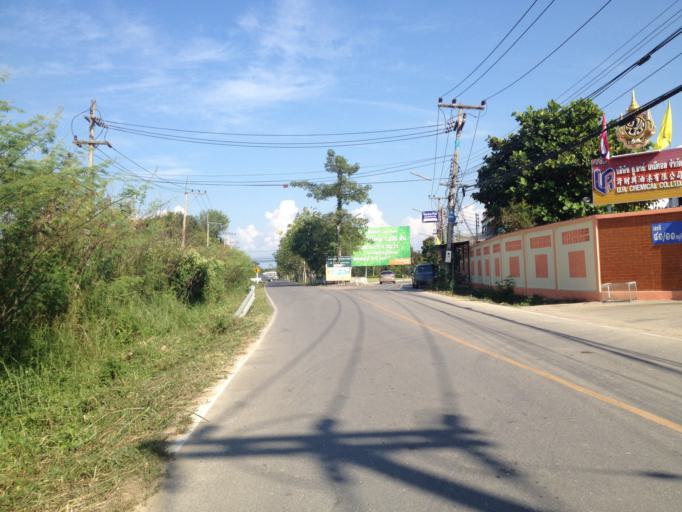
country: TH
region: Chiang Mai
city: Chiang Mai
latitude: 18.7344
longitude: 98.9634
